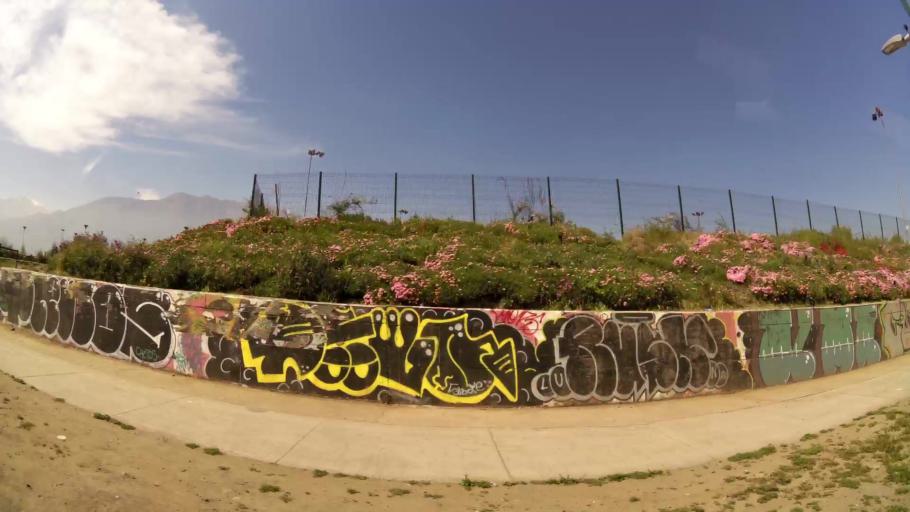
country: CL
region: Santiago Metropolitan
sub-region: Provincia de Santiago
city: Villa Presidente Frei, Nunoa, Santiago, Chile
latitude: -33.4646
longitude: -70.5483
